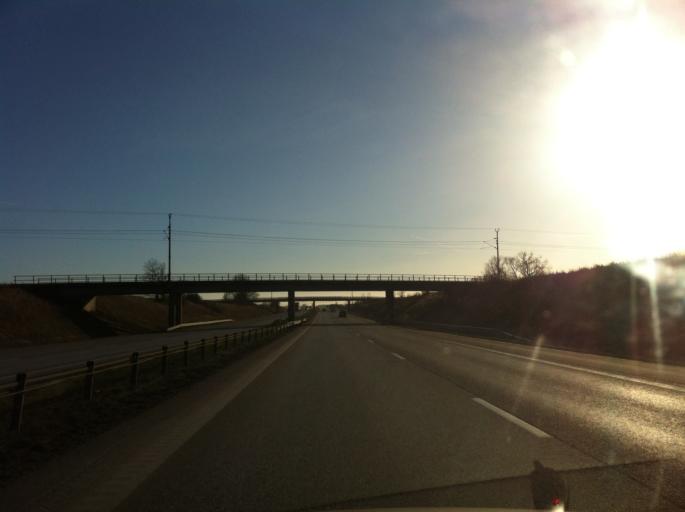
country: SE
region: Skane
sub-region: Angelholms Kommun
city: Strovelstorp
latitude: 56.1353
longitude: 12.8361
